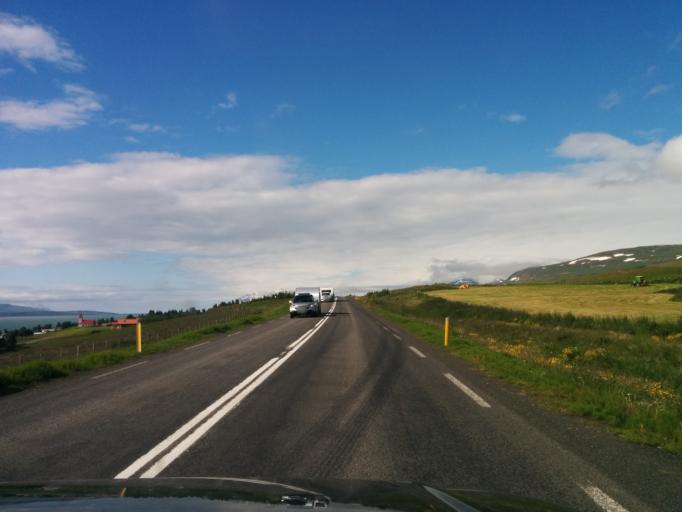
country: IS
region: Northeast
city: Akureyri
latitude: 65.7391
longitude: -18.0739
